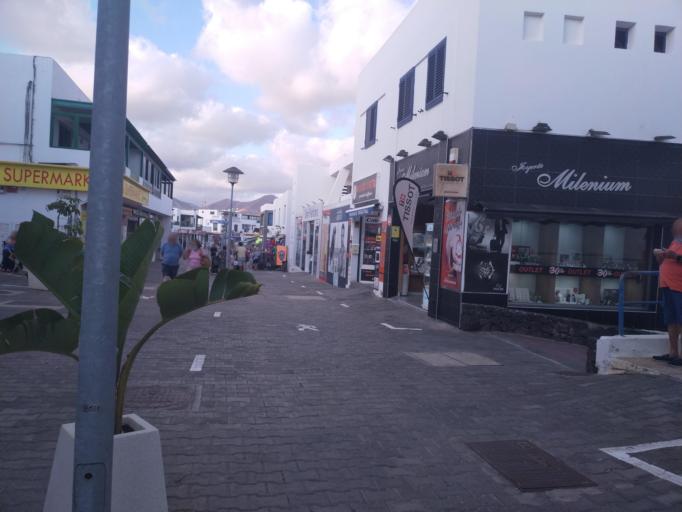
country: ES
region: Canary Islands
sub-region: Provincia de Las Palmas
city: Playa Blanca
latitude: 28.8624
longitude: -13.8309
